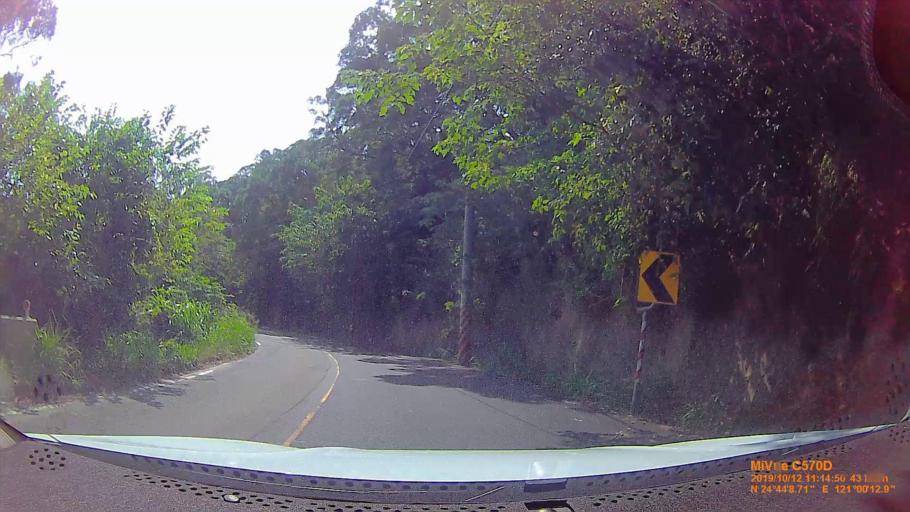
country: TW
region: Taiwan
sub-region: Hsinchu
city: Hsinchu
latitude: 24.7357
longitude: 121.0036
